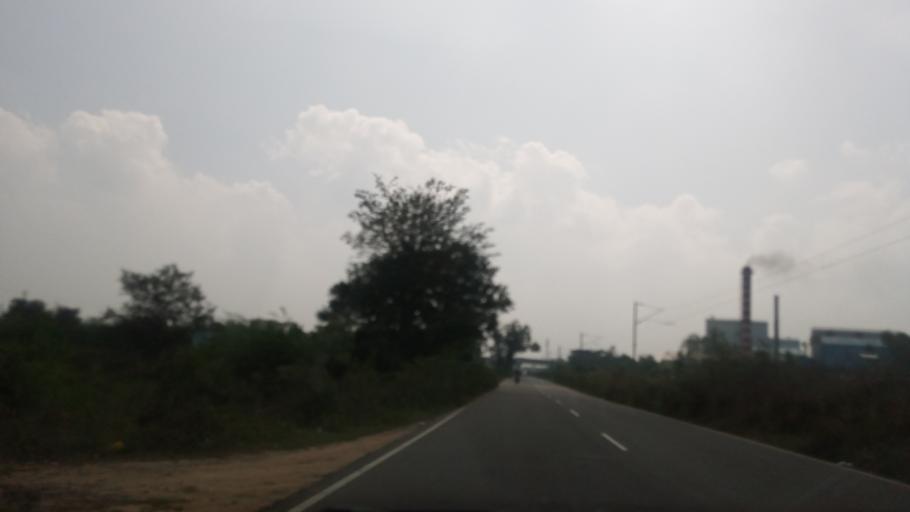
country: IN
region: Tamil Nadu
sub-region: Kancheepuram
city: Kanchipuram
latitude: 12.8789
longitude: 79.6895
